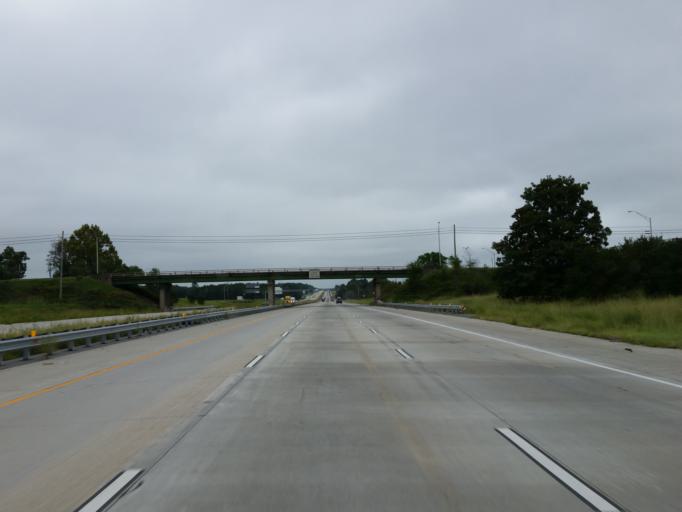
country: US
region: Georgia
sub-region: Dooly County
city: Vienna
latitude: 32.0880
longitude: -83.7633
